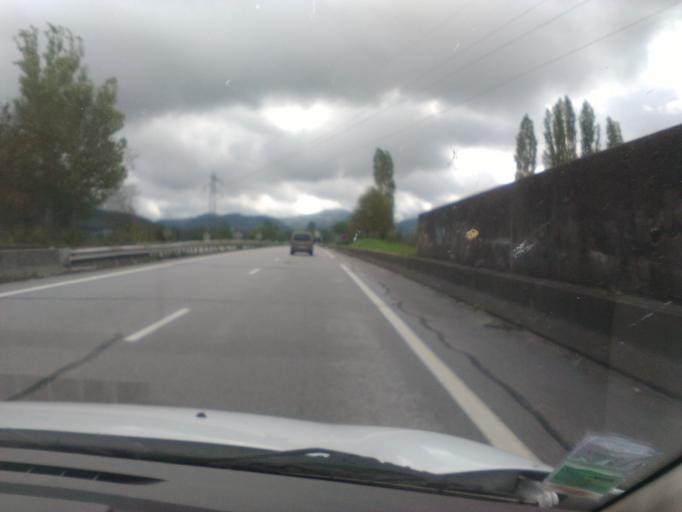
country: FR
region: Lorraine
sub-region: Departement des Vosges
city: Saint-Etienne-les-Remiremont
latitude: 48.0180
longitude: 6.5994
